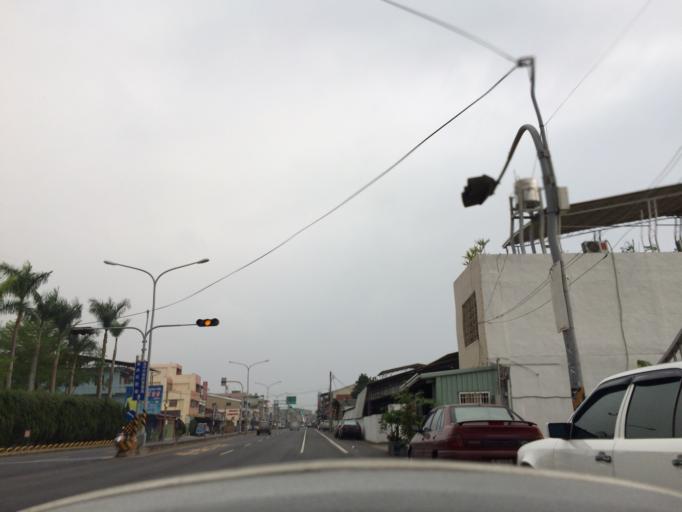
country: TW
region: Taiwan
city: Zhongxing New Village
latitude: 24.0282
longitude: 120.6968
